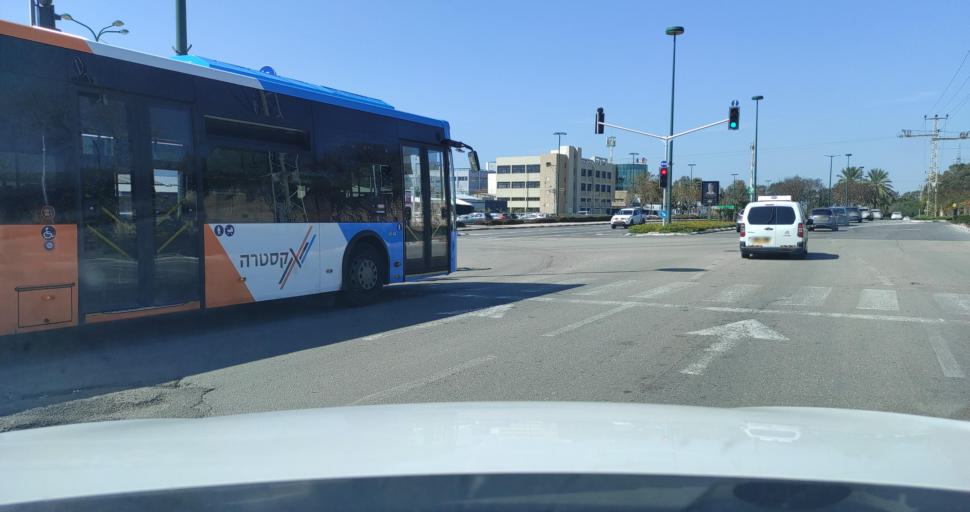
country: IL
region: Central District
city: Bet Yizhaq
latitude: 32.3194
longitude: 34.8827
